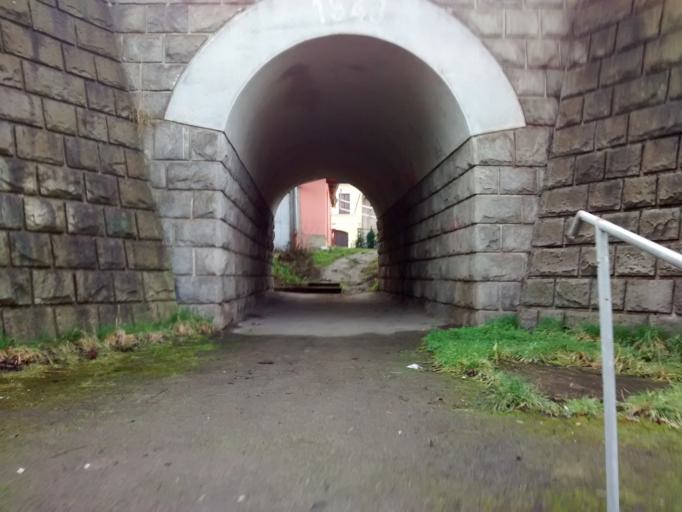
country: CZ
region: Ustecky
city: Roudnice nad Labem
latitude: 50.4278
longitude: 14.2544
